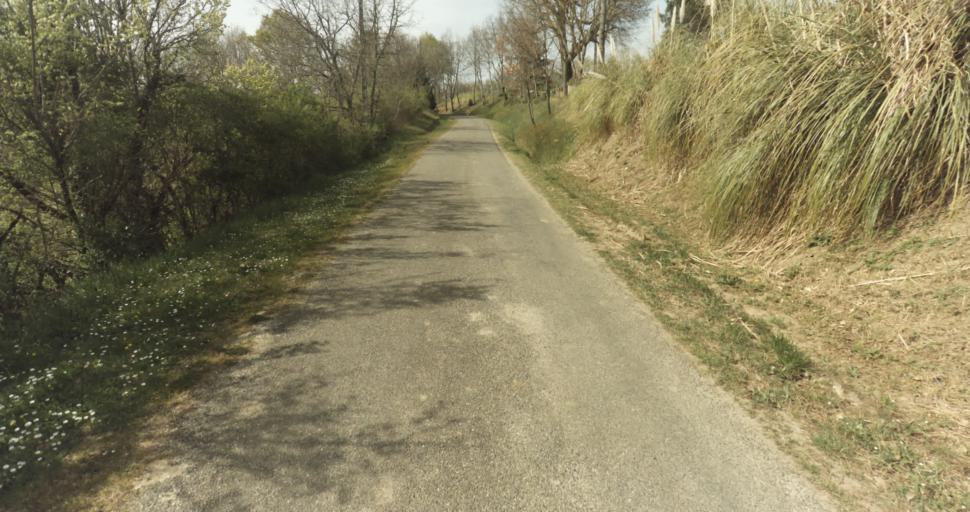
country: FR
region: Midi-Pyrenees
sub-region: Departement du Tarn-et-Garonne
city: Moissac
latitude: 44.1427
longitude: 1.1490
